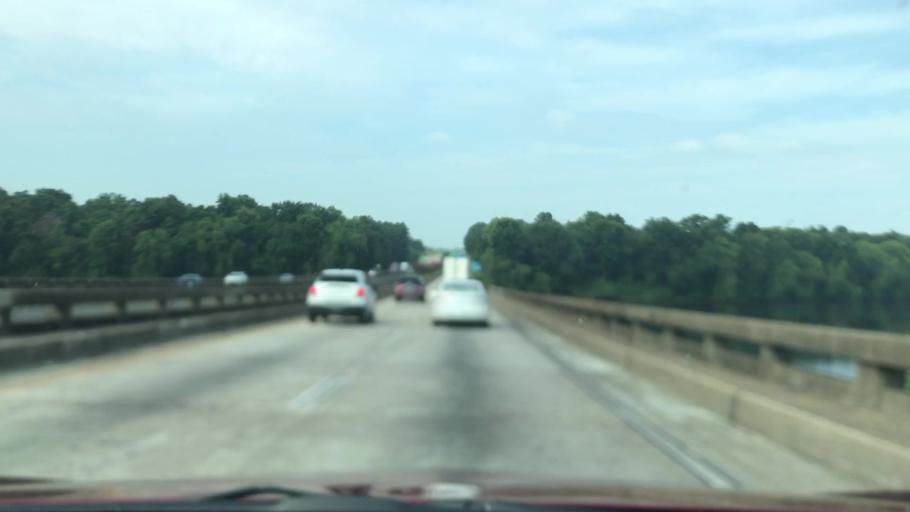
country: US
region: South Carolina
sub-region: Aiken County
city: North Augusta
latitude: 33.5325
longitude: -82.0107
